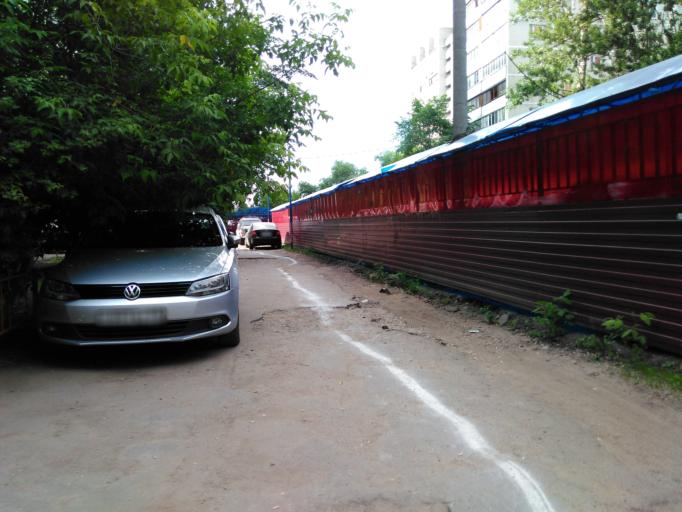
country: RU
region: Moskovskaya
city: Reutov
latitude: 55.7477
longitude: 37.8636
